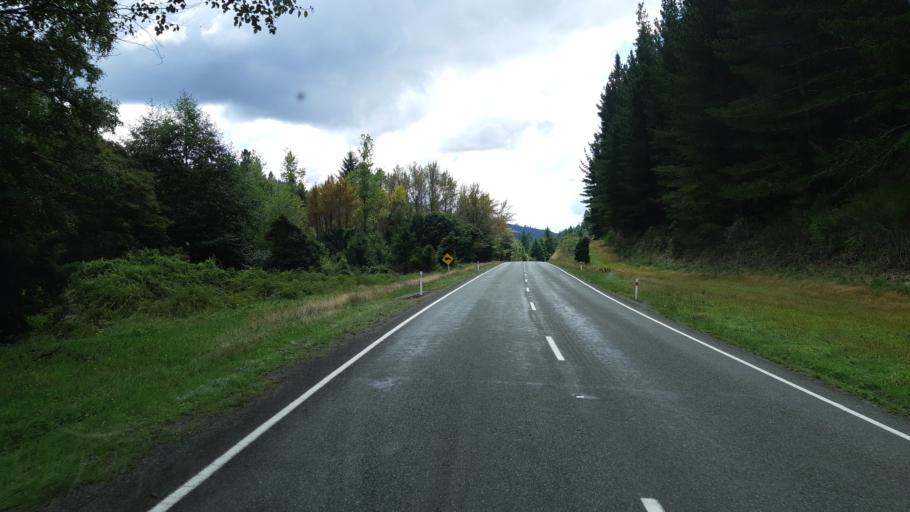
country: NZ
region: Tasman
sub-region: Tasman District
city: Wakefield
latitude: -41.5884
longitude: 172.7646
